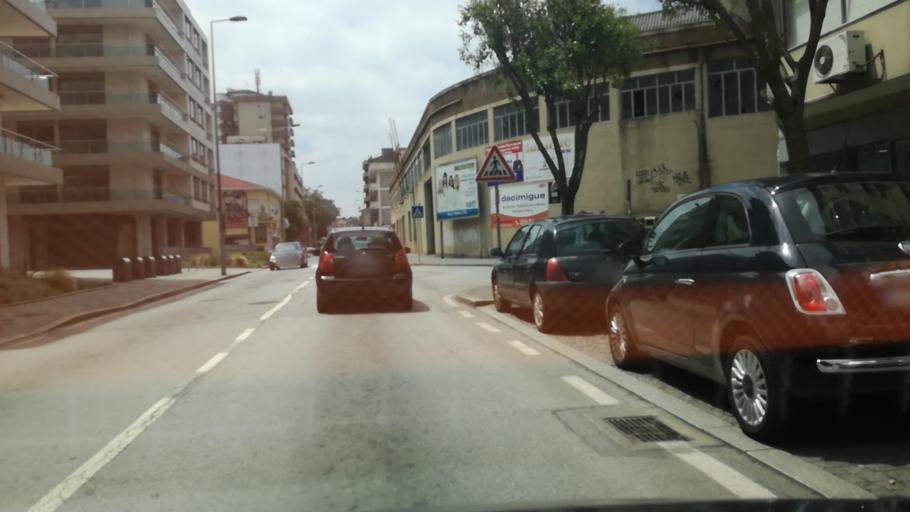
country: PT
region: Porto
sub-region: Trofa
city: Bougado
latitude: 41.3396
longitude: -8.5586
